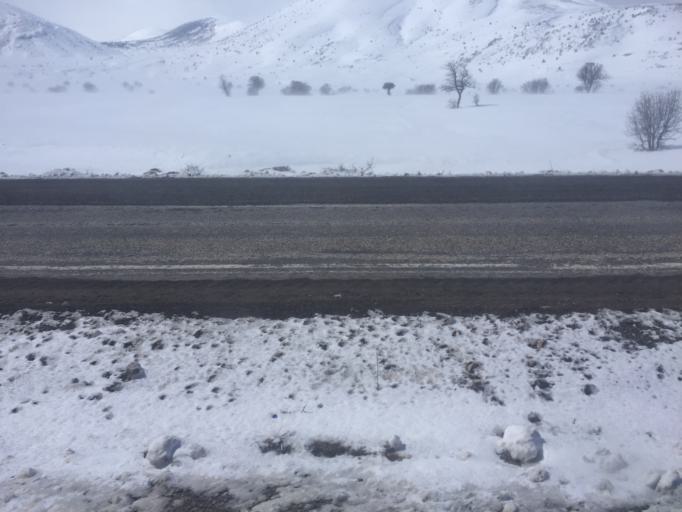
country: TR
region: Kahramanmaras
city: Goksun
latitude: 38.1788
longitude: 36.4586
